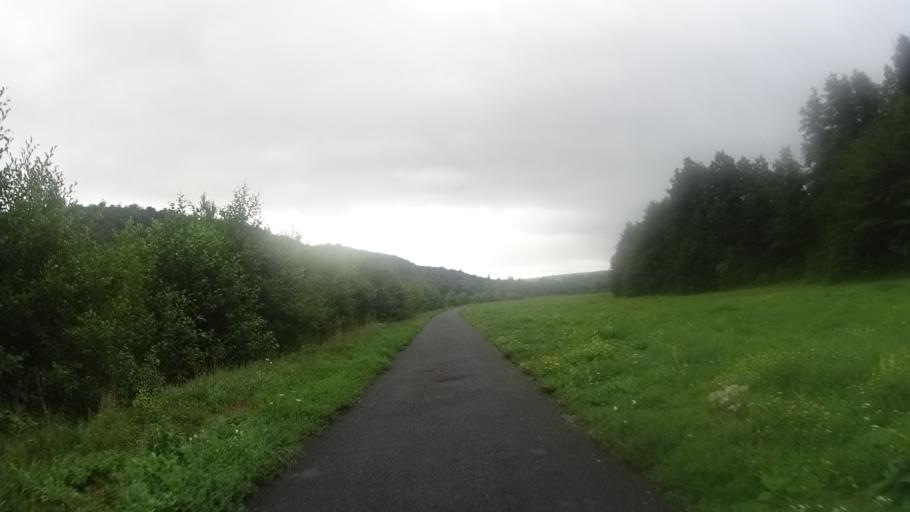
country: FR
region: Lorraine
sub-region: Departement de Meurthe-et-Moselle
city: Chaligny
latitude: 48.6492
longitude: 6.0389
